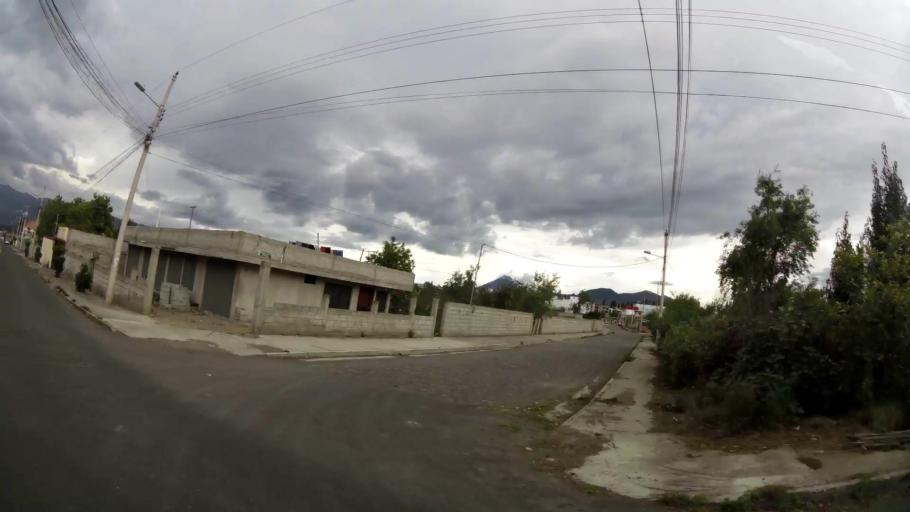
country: EC
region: Tungurahua
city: Ambato
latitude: -1.2775
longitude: -78.6212
